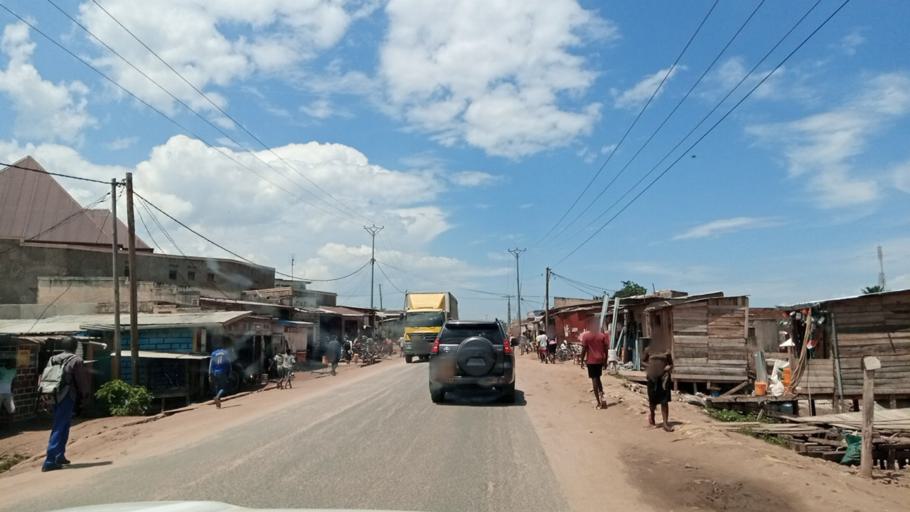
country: BI
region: Bujumbura Mairie
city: Bujumbura
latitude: -3.4229
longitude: 29.3563
